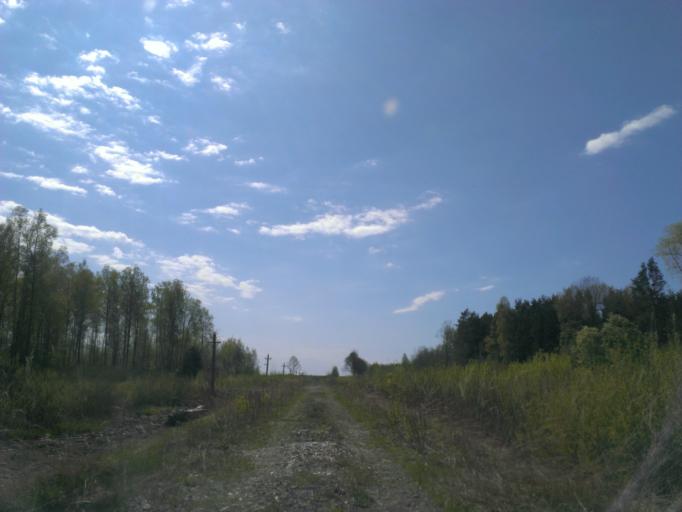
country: LV
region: Saulkrastu
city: Saulkrasti
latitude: 57.3425
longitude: 24.4794
